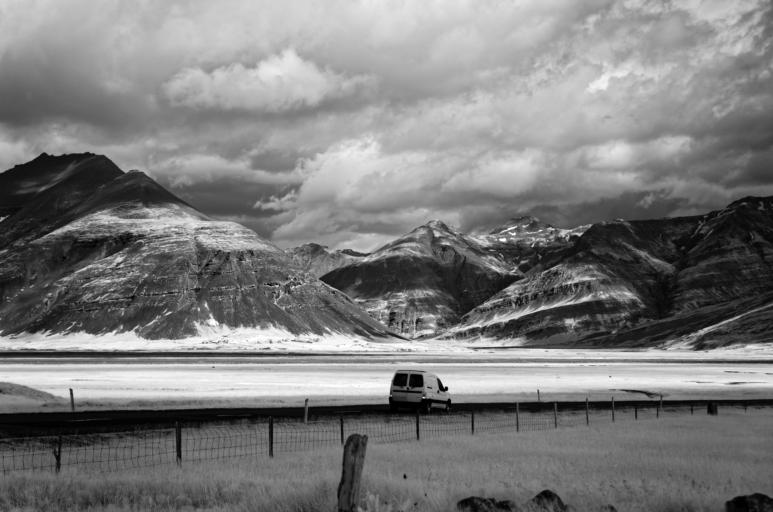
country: IS
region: East
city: Hoefn
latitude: 64.3479
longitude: -15.3930
